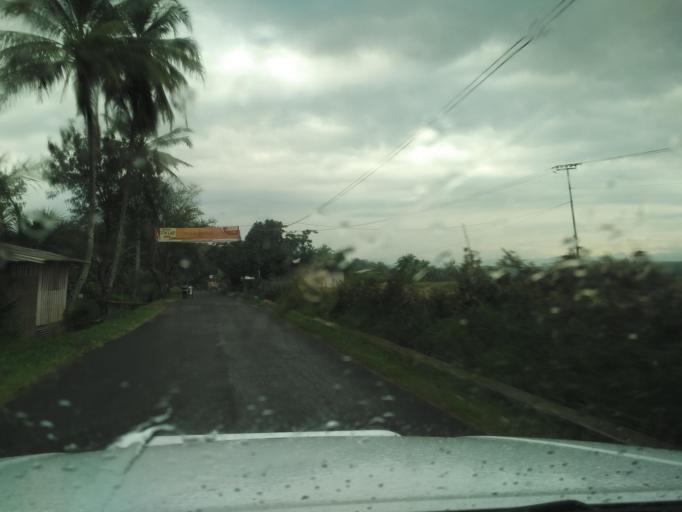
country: ID
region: West Java
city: Ciranjang-hilir
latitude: -6.7037
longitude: 107.1828
